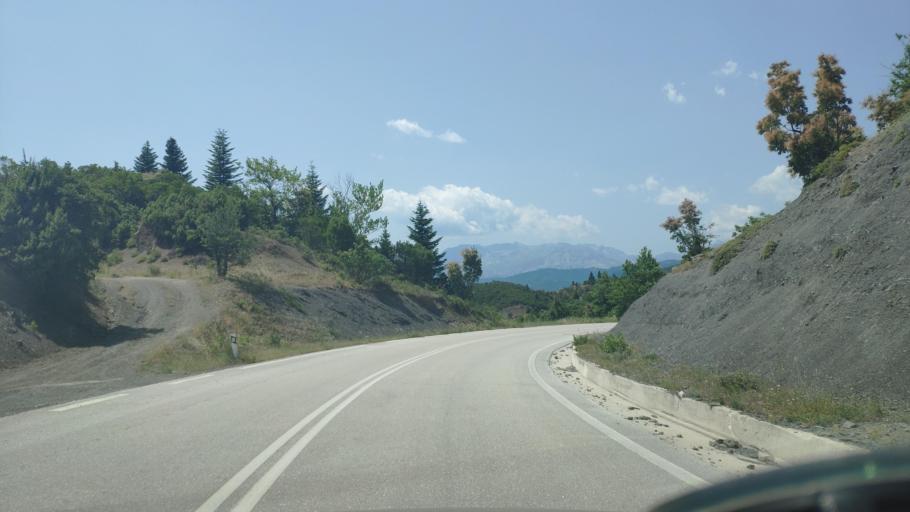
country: GR
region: Epirus
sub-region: Nomos Artas
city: Ano Kalentini
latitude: 39.2837
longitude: 21.3190
